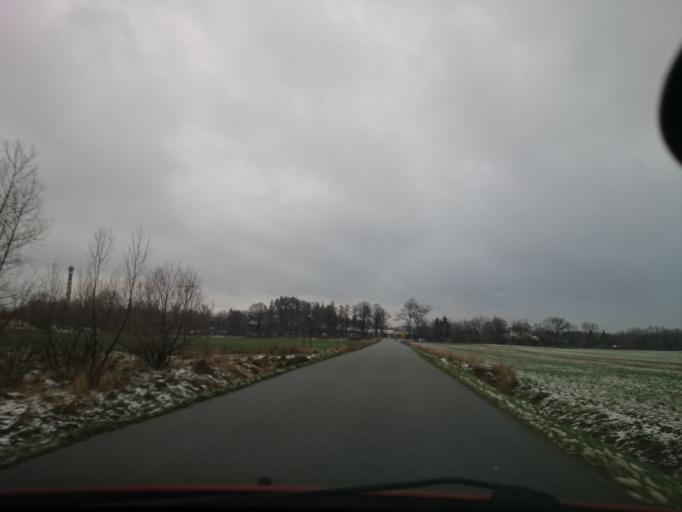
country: PL
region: Lower Silesian Voivodeship
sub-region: Powiat klodzki
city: Klodzko
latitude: 50.4119
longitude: 16.6387
